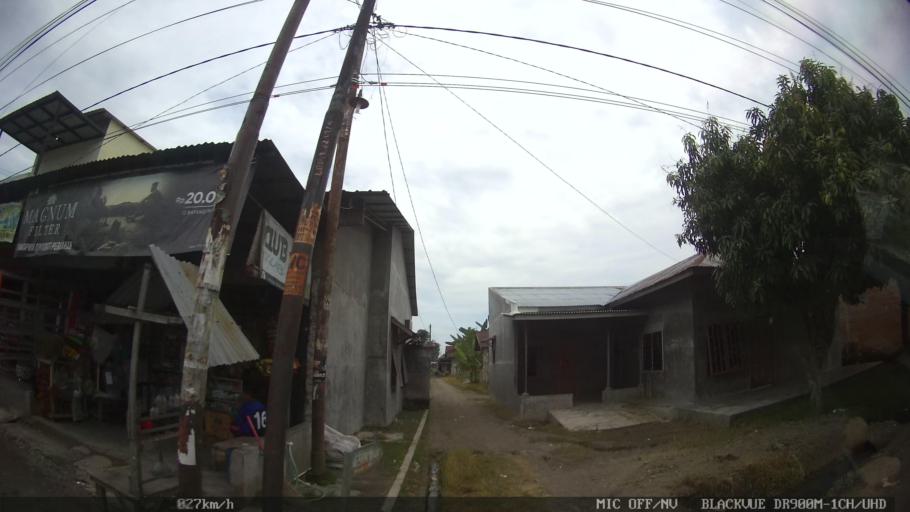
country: ID
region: North Sumatra
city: Binjai
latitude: 3.6299
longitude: 98.5554
